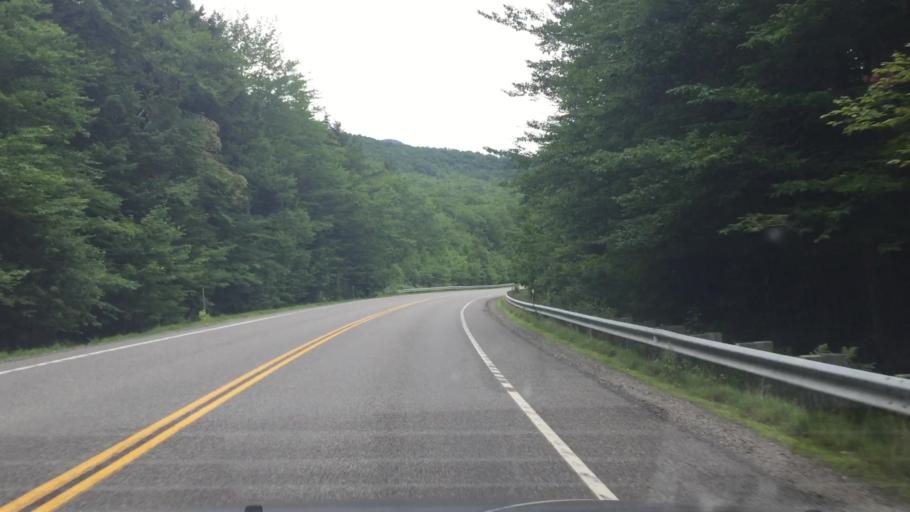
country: US
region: New Hampshire
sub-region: Carroll County
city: North Conway
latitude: 44.0880
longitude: -71.3527
